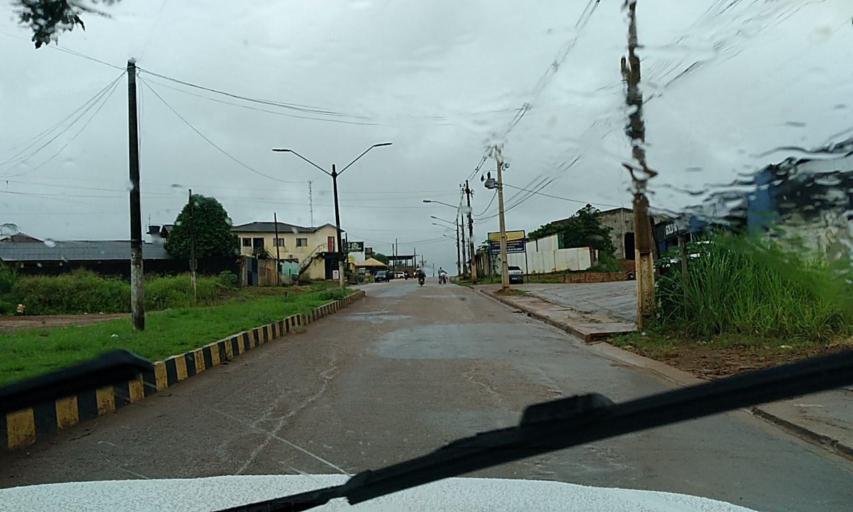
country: BR
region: Para
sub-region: Altamira
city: Altamira
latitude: -3.2131
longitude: -52.2336
